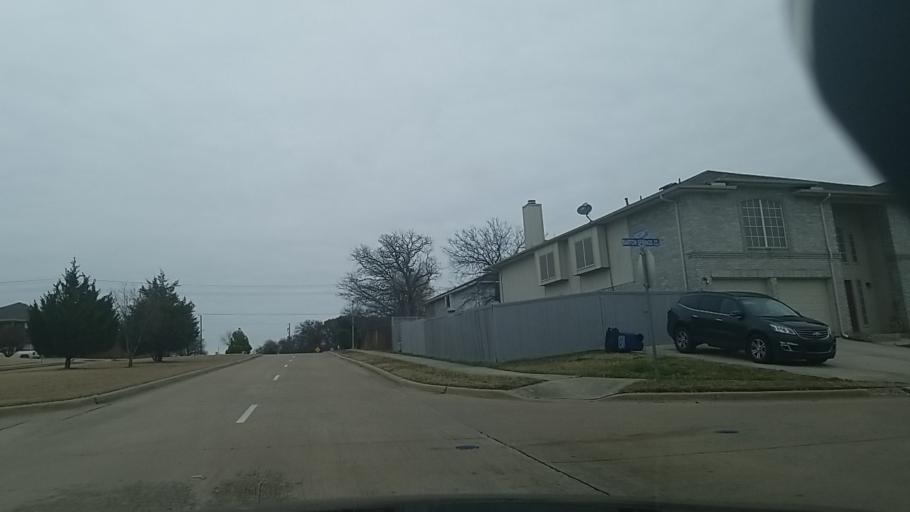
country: US
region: Texas
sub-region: Denton County
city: Corinth
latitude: 33.1409
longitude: -97.0786
